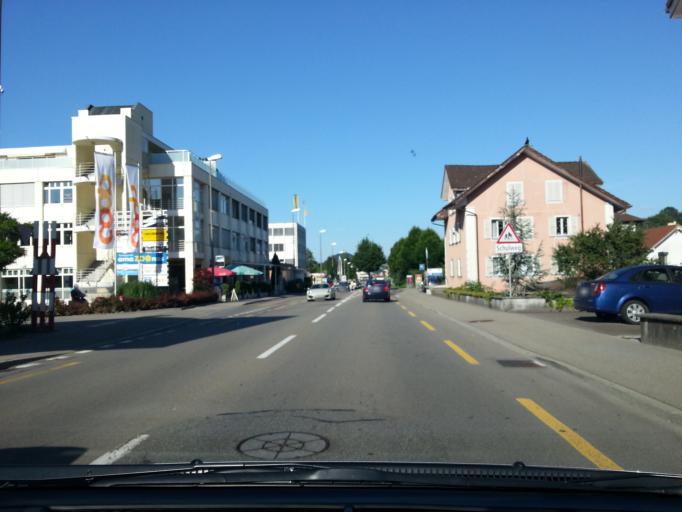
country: CH
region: Lucerne
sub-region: Lucerne-Stadt District
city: Littau
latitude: 47.0507
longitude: 8.2703
